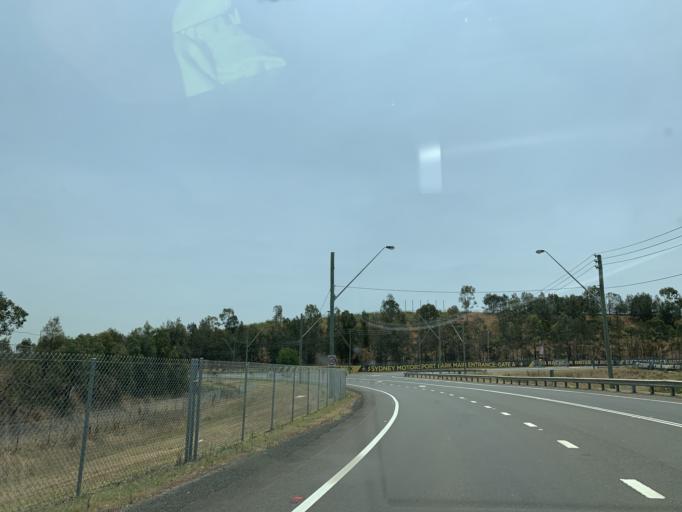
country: AU
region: New South Wales
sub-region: Fairfield
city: Horsley Park
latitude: -33.8107
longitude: 150.8663
